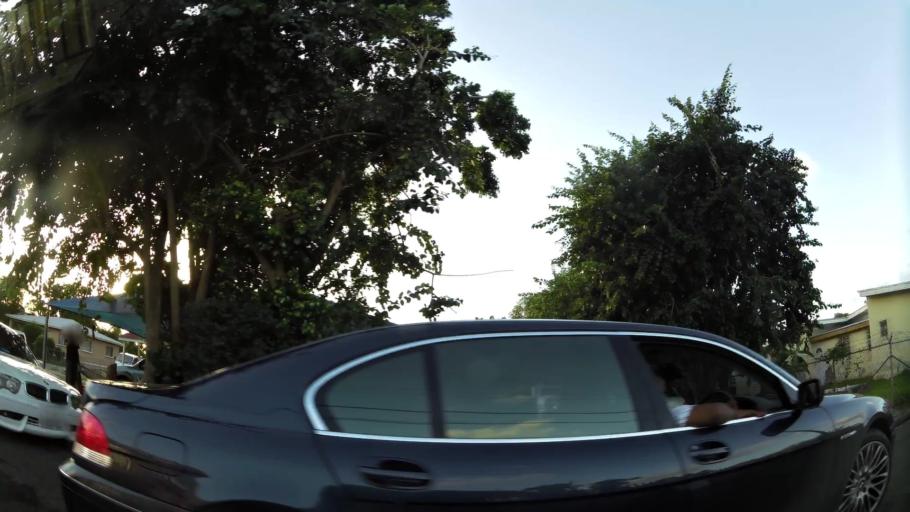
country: AG
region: Saint John
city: Saint John's
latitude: 17.1286
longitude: -61.8413
